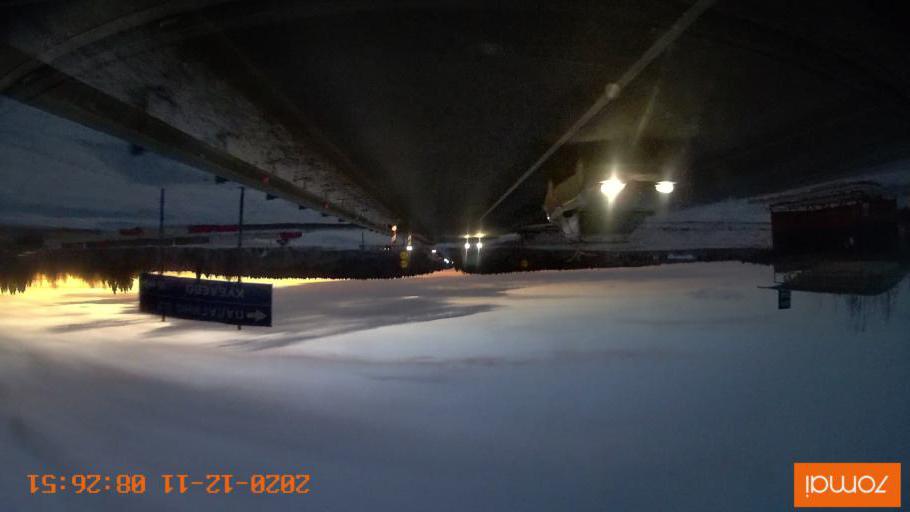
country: RU
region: Vologda
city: Molochnoye
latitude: 59.1712
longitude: 39.4750
